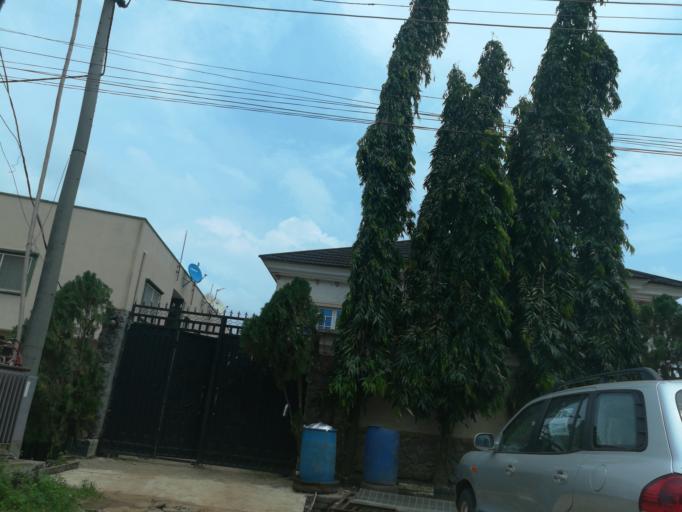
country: NG
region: Lagos
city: Oshodi
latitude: 6.5534
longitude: 3.3245
